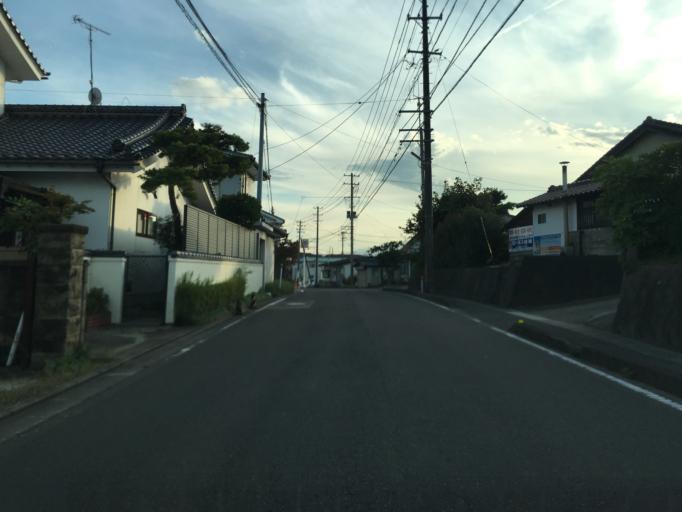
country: JP
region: Fukushima
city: Hobaramachi
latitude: 37.8278
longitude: 140.5047
